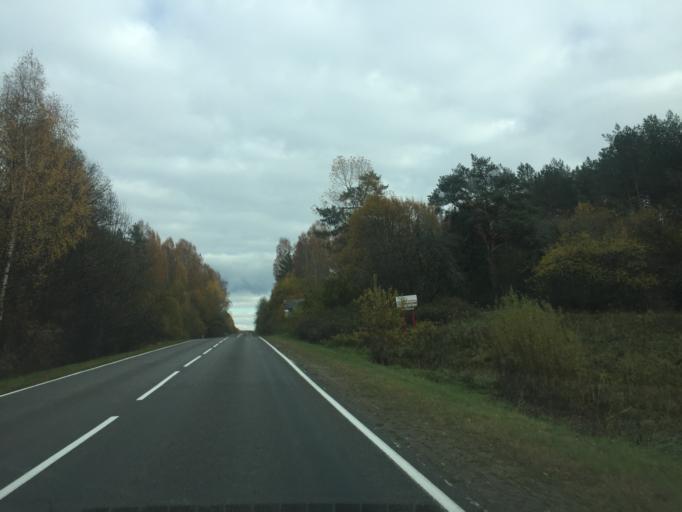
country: BY
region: Minsk
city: Svir
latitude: 54.8730
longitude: 26.3536
